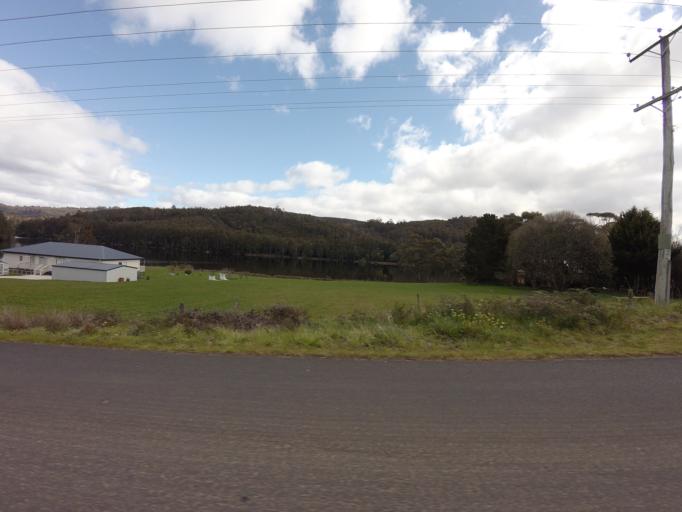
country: AU
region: Tasmania
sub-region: Huon Valley
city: Geeveston
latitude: -43.1868
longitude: 146.9331
